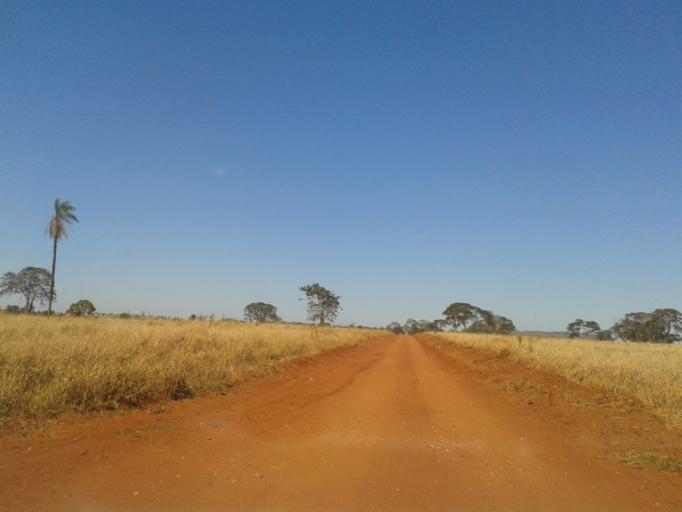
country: BR
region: Minas Gerais
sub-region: Santa Vitoria
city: Santa Vitoria
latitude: -19.1566
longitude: -50.1563
